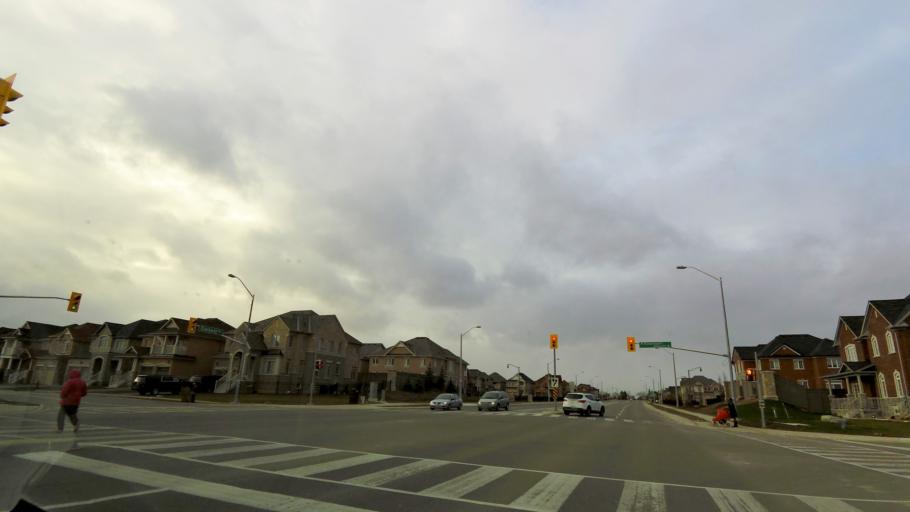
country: CA
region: Ontario
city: Brampton
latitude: 43.7977
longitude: -79.6740
